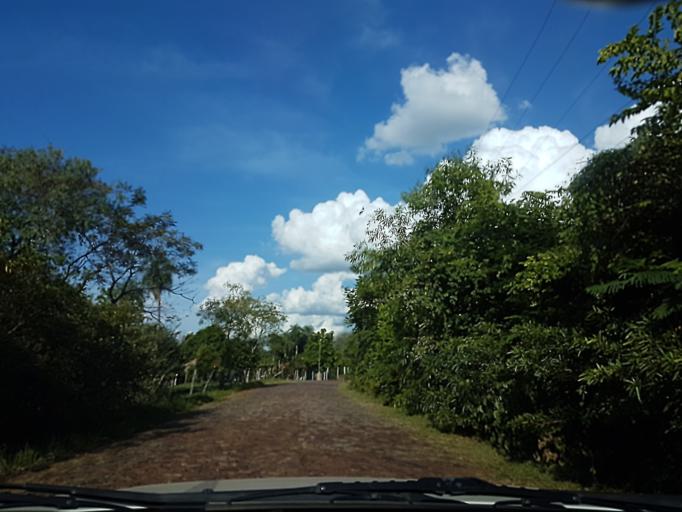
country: PY
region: Cordillera
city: Arroyos y Esteros
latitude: -24.9976
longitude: -57.1398
